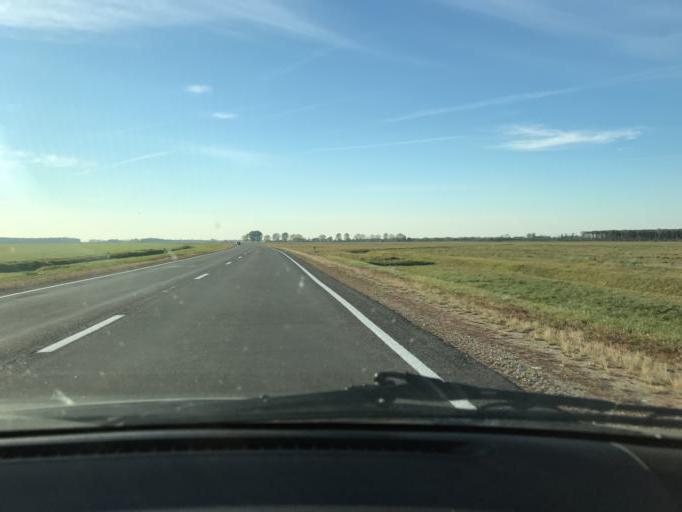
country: BY
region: Brest
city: Antopal'
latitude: 52.2268
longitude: 24.8139
